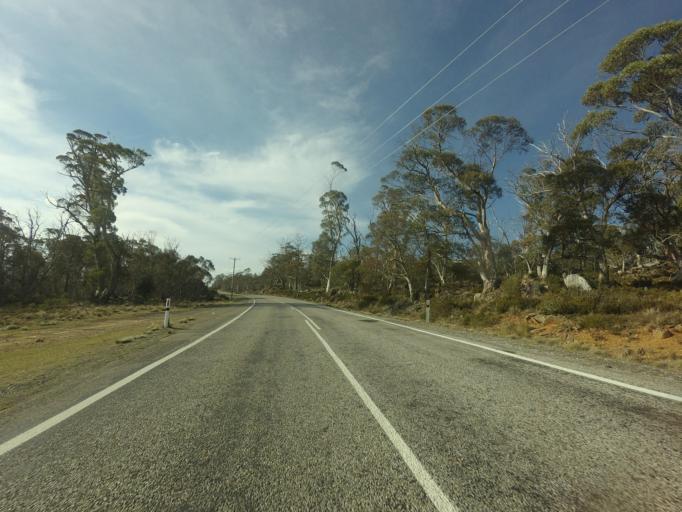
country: AU
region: Tasmania
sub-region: Meander Valley
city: Deloraine
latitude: -41.9920
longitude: 146.7077
